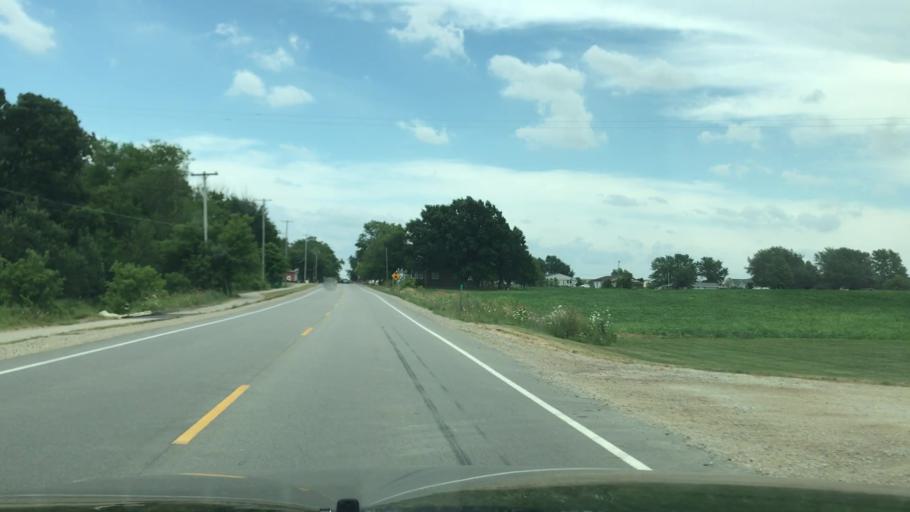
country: US
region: Michigan
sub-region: Ottawa County
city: Zeeland
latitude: 42.7829
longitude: -85.9446
